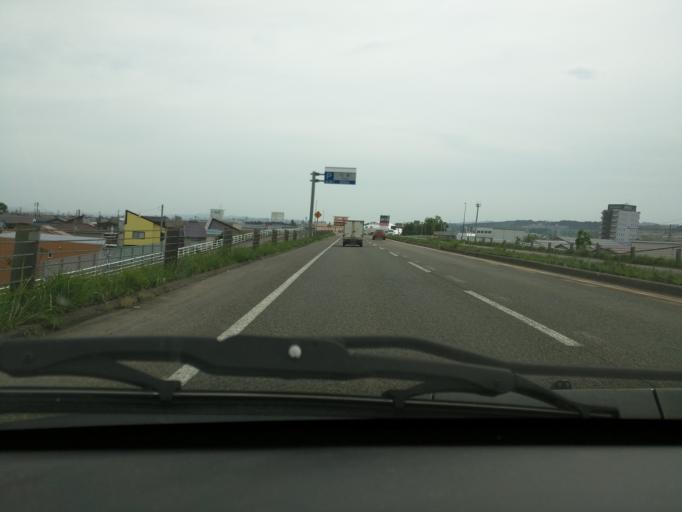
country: JP
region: Niigata
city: Nagaoka
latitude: 37.4507
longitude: 138.8010
